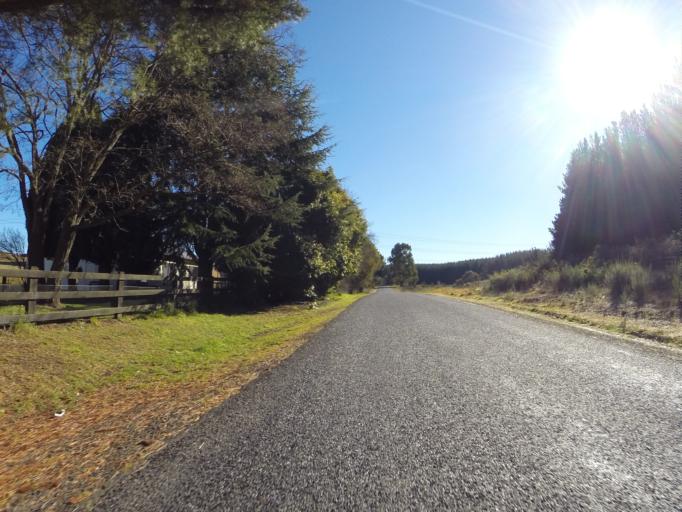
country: AU
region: New South Wales
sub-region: Oberon
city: Oberon
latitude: -33.6542
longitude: 149.8538
